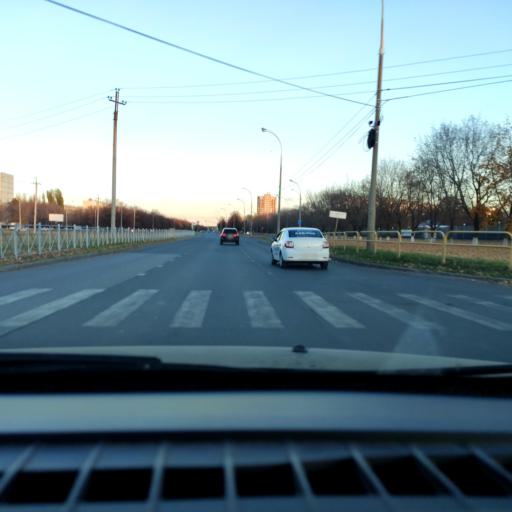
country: RU
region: Samara
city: Tol'yatti
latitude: 53.5195
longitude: 49.2796
